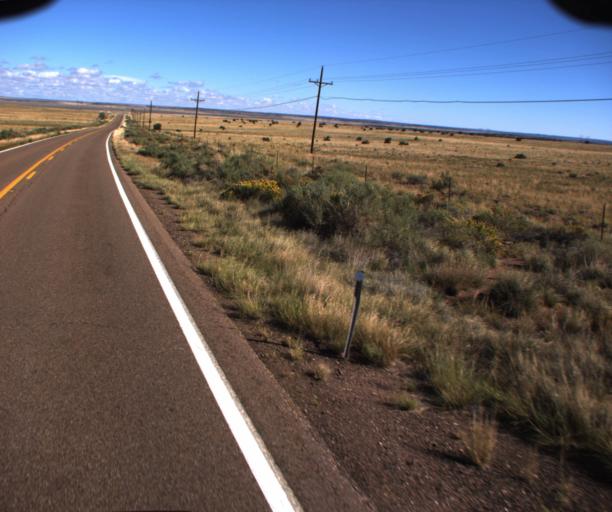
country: US
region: Arizona
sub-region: Apache County
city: Saint Johns
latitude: 34.5604
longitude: -109.3418
